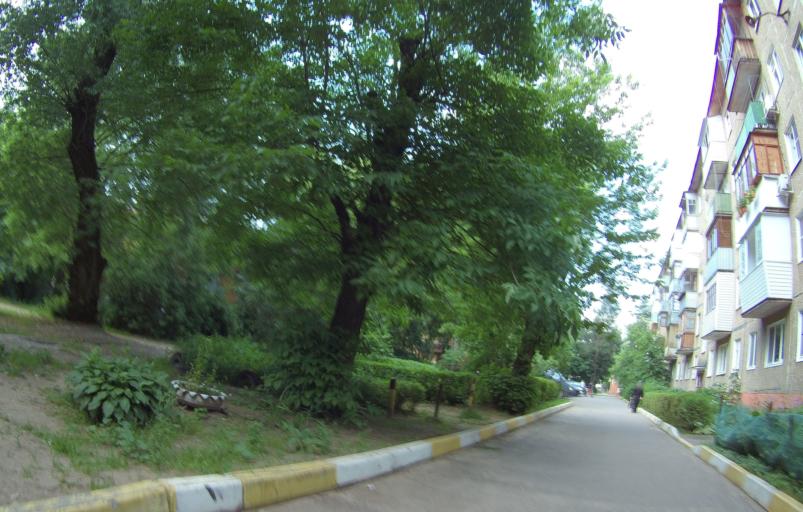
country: RU
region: Moskovskaya
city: Vereya
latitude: 55.6292
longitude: 38.0510
